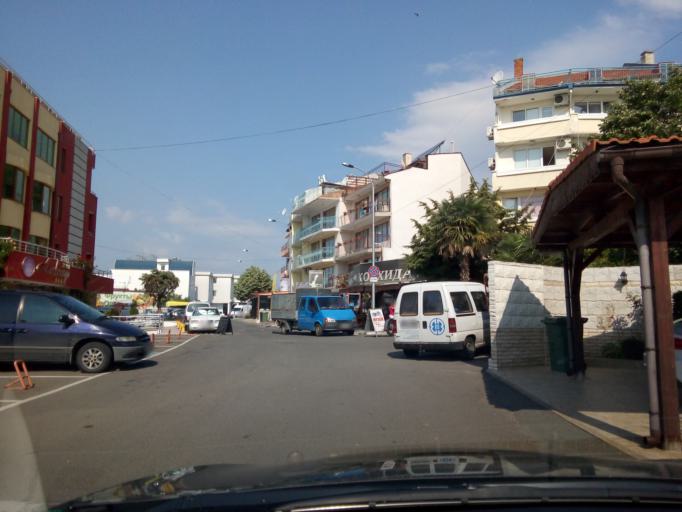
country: BG
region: Burgas
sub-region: Obshtina Nesebur
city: Sveti Vlas
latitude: 42.7115
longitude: 27.7668
